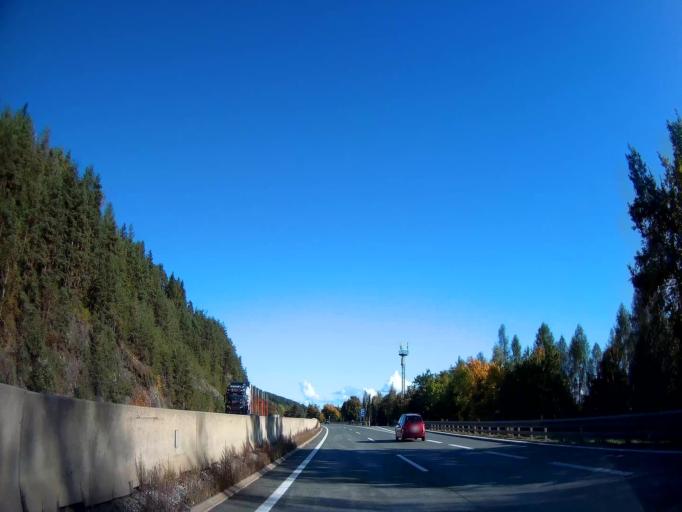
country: AT
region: Carinthia
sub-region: Politischer Bezirk Klagenfurt Land
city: Maria Worth
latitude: 46.6343
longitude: 14.1667
